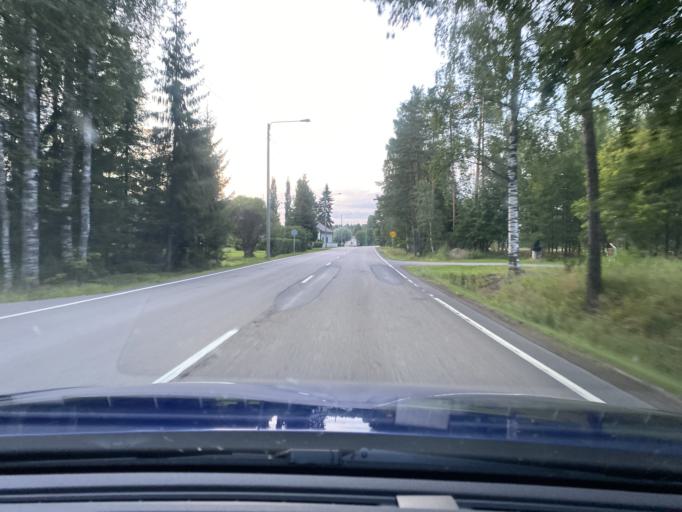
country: FI
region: Satakunta
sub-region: Pohjois-Satakunta
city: Honkajoki
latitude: 61.9631
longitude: 22.2212
